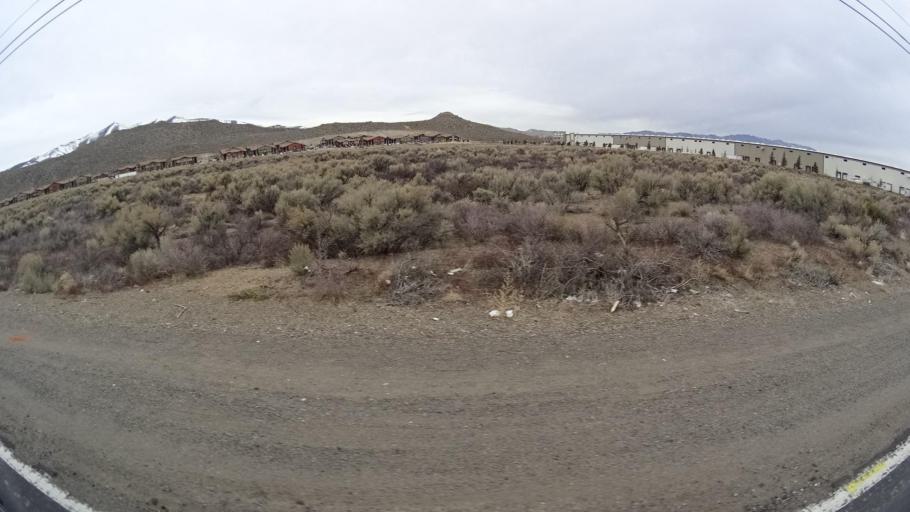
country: US
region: Nevada
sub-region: Washoe County
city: Lemmon Valley
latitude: 39.6278
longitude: -119.8469
